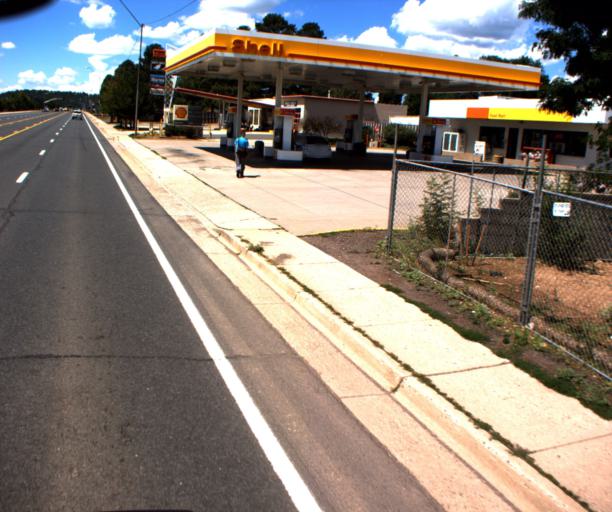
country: US
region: Arizona
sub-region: Coconino County
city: Flagstaff
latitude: 35.2126
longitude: -111.6016
